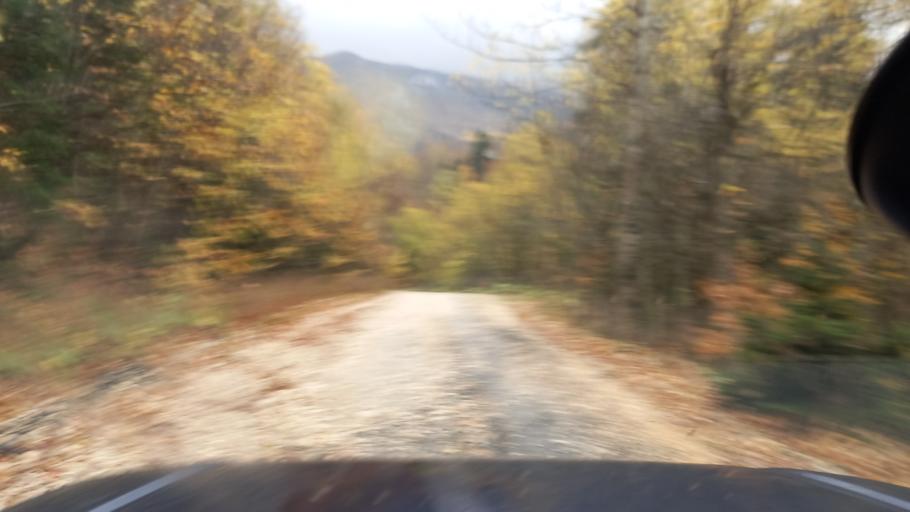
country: RU
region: Krasnodarskiy
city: Neftegorsk
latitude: 44.0190
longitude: 39.8435
